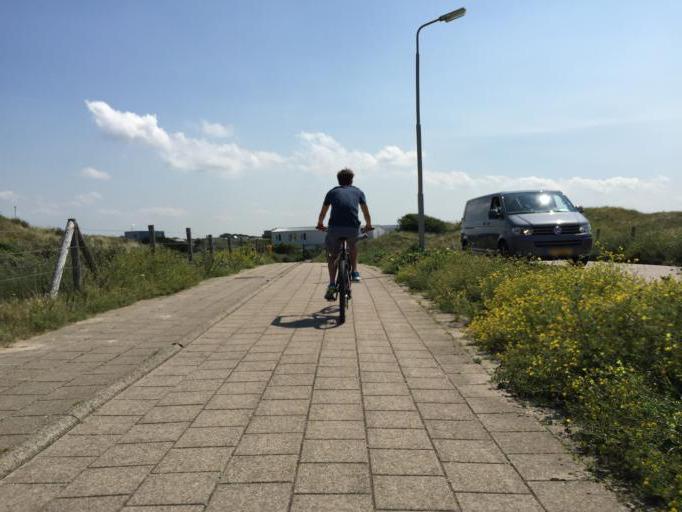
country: NL
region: North Holland
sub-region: Gemeente Bloemendaal
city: Bloemendaal
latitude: 52.4562
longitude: 4.5716
